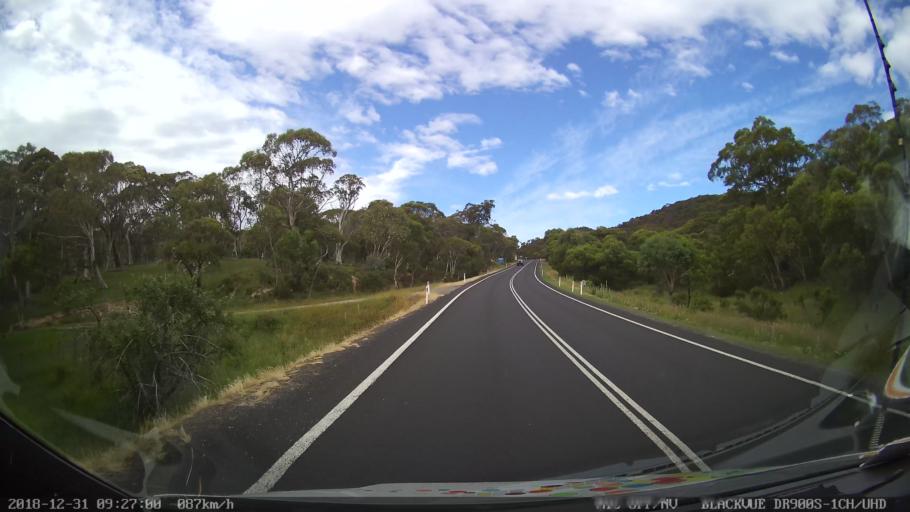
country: AU
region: New South Wales
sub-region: Snowy River
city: Jindabyne
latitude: -36.4539
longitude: 148.4907
